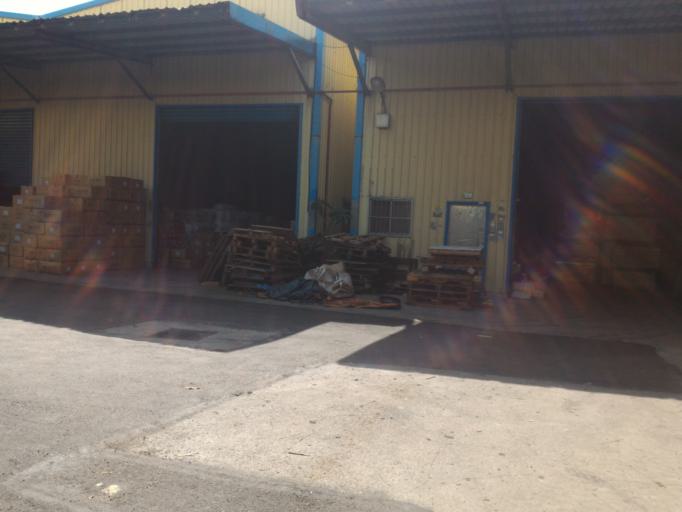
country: TW
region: Taiwan
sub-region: Taoyuan
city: Taoyuan
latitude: 24.9605
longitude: 121.3990
